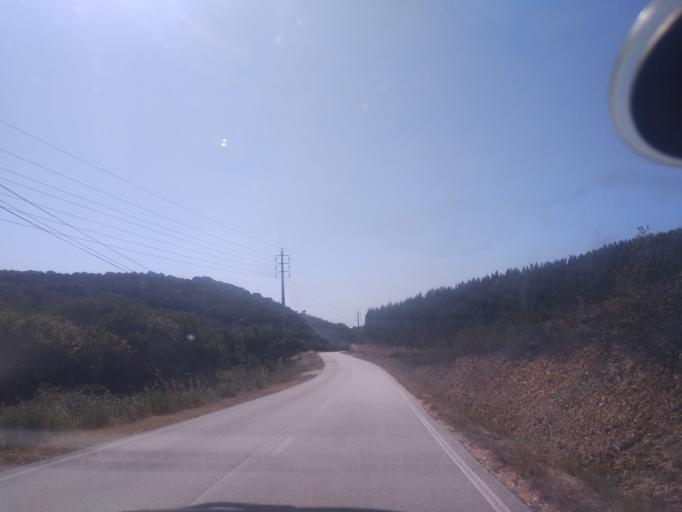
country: PT
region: Faro
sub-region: Aljezur
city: Aljezur
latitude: 37.2160
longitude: -8.7867
